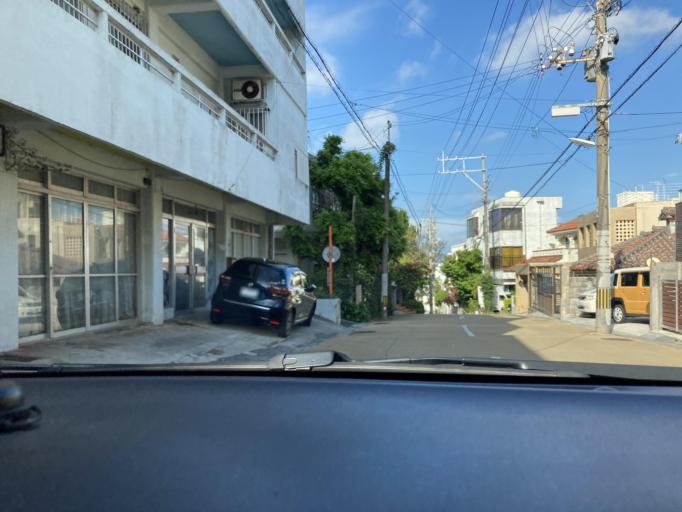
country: JP
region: Okinawa
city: Naha-shi
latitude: 26.2190
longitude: 127.7122
